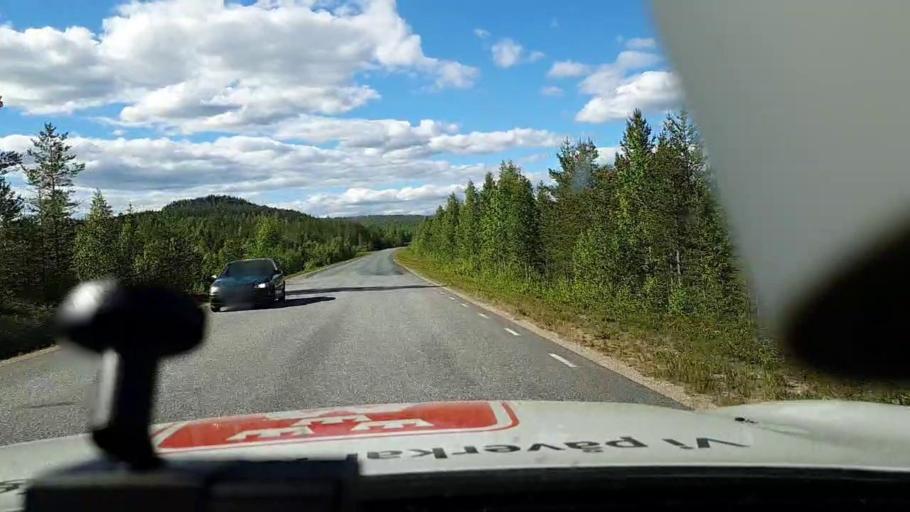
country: FI
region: Lapland
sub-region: Torniolaakso
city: Ylitornio
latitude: 66.3014
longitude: 23.6314
